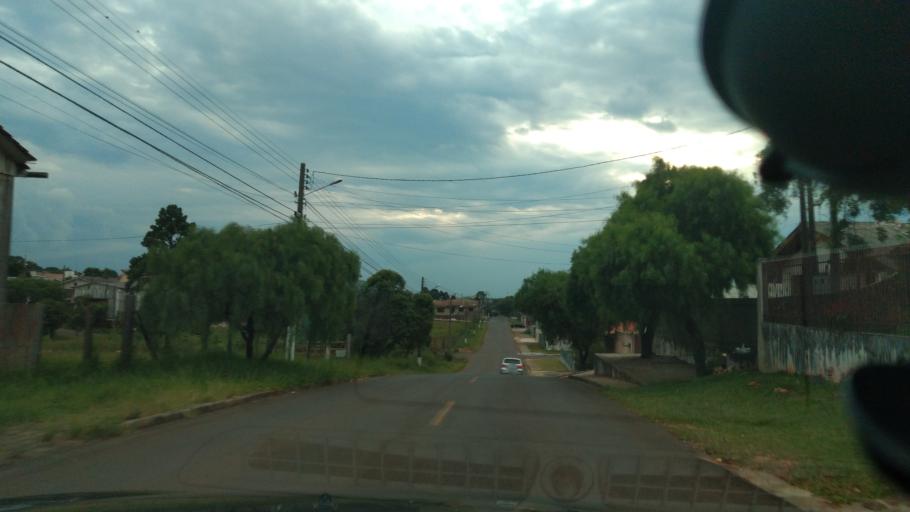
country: BR
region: Parana
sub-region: Guarapuava
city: Guarapuava
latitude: -25.3865
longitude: -51.4809
